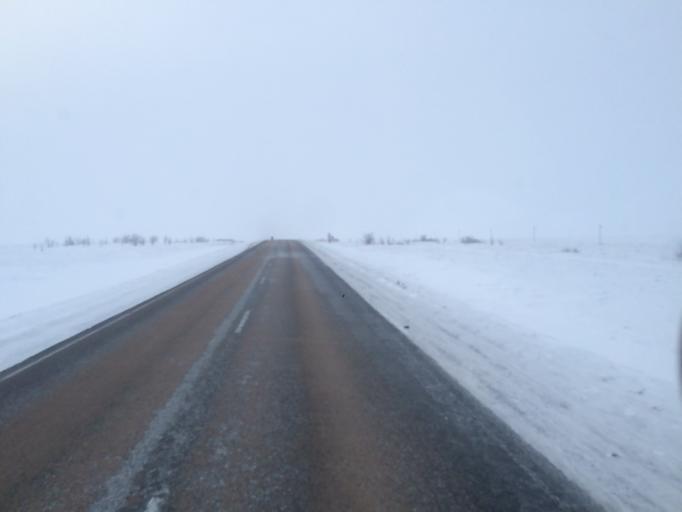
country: RU
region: Orenburg
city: Dombarovskiy
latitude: 50.0928
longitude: 59.4979
